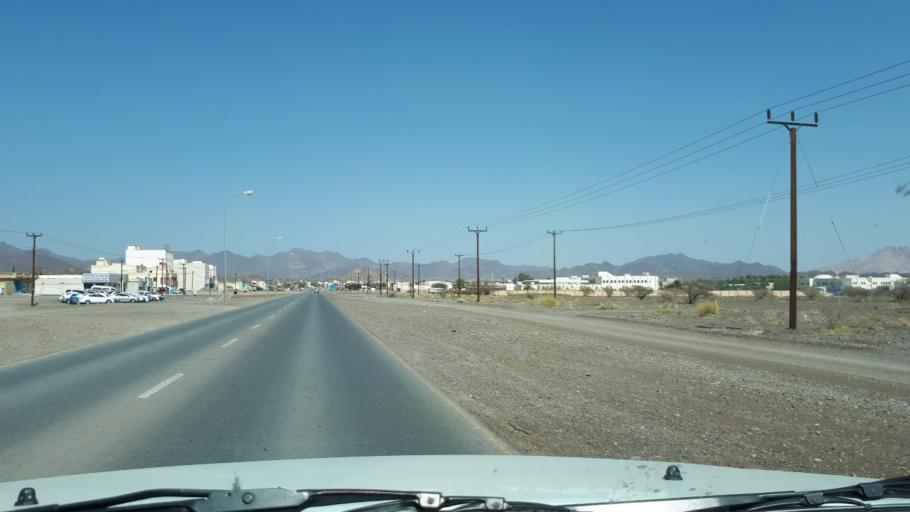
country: OM
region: Muhafazat ad Dakhiliyah
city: Bahla'
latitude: 22.9474
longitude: 57.2691
